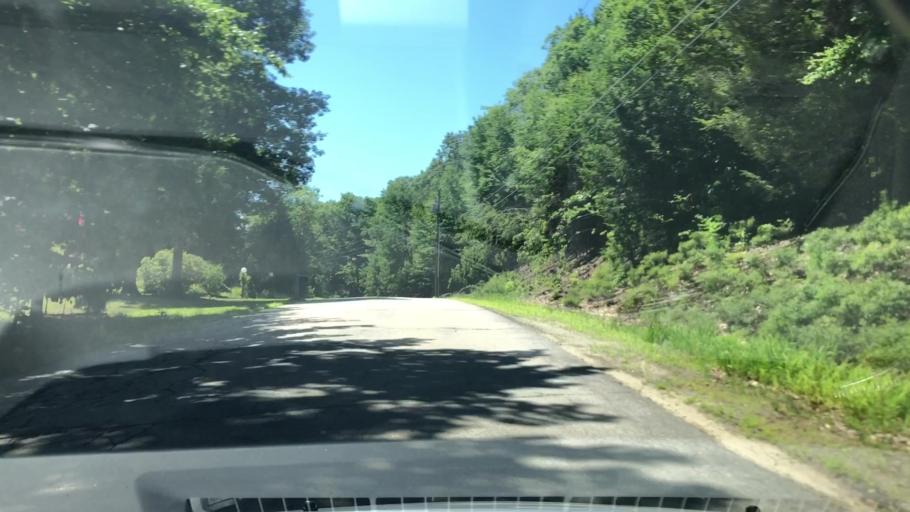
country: US
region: New Hampshire
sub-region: Hillsborough County
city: Mont Vernon
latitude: 42.9035
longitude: -71.6099
